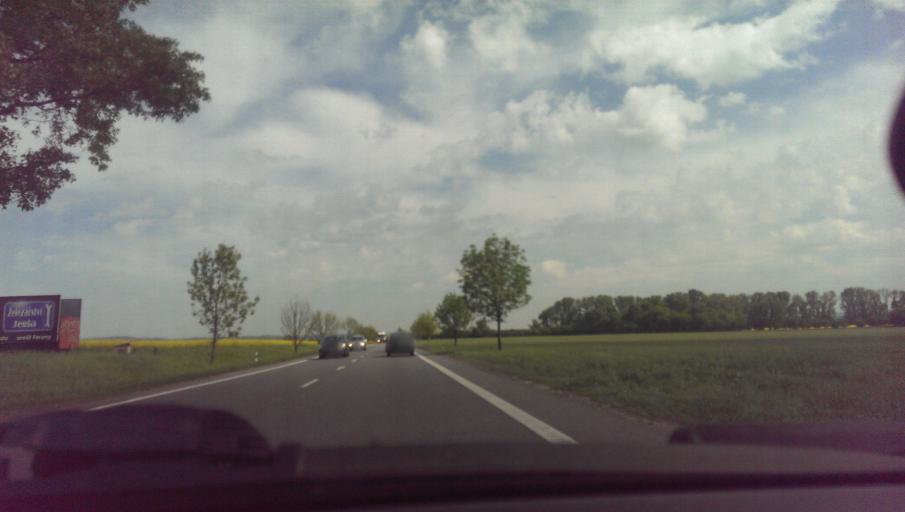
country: CZ
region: Zlin
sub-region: Okres Uherske Hradiste
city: Uherske Hradiste
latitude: 49.0942
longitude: 17.4525
